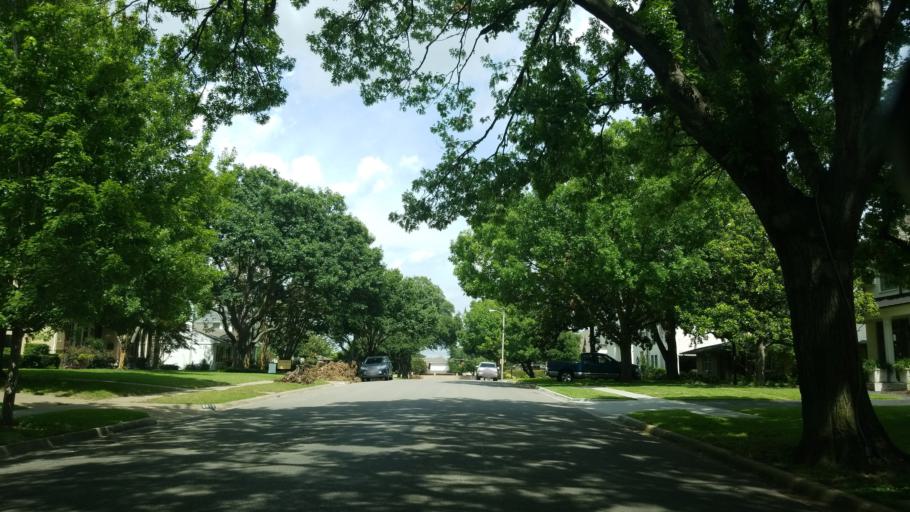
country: US
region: Texas
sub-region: Dallas County
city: University Park
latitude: 32.8706
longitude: -96.7887
